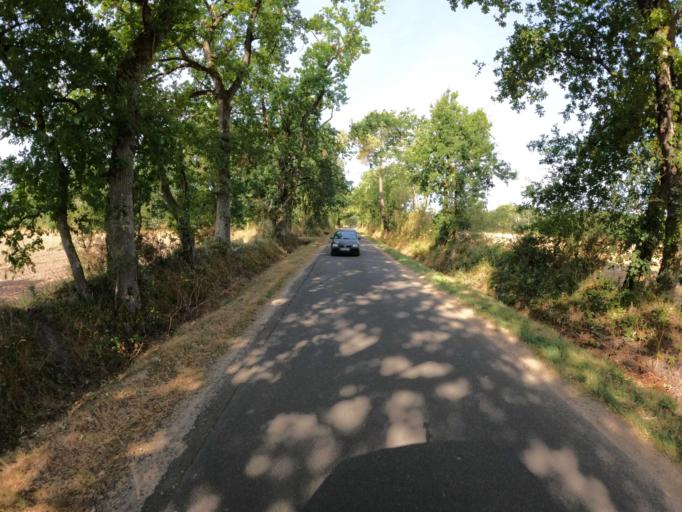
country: FR
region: Pays de la Loire
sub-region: Departement de la Vendee
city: Challans
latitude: 46.8075
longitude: -1.8495
